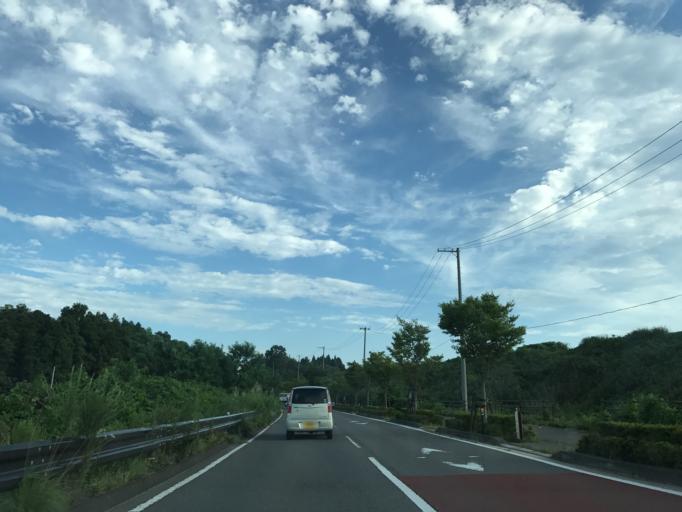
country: JP
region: Fukushima
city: Koriyama
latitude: 37.3567
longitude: 140.3259
